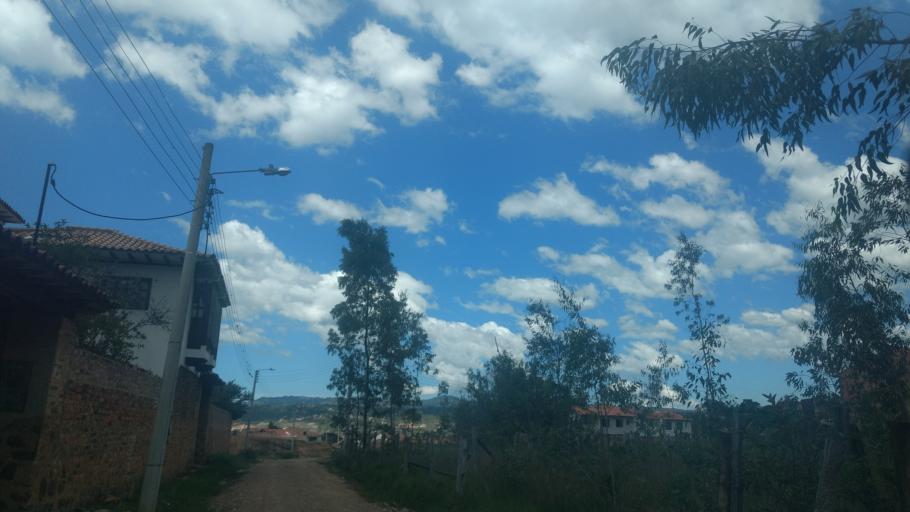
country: CO
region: Boyaca
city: Sachica
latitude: 5.6257
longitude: -73.5255
